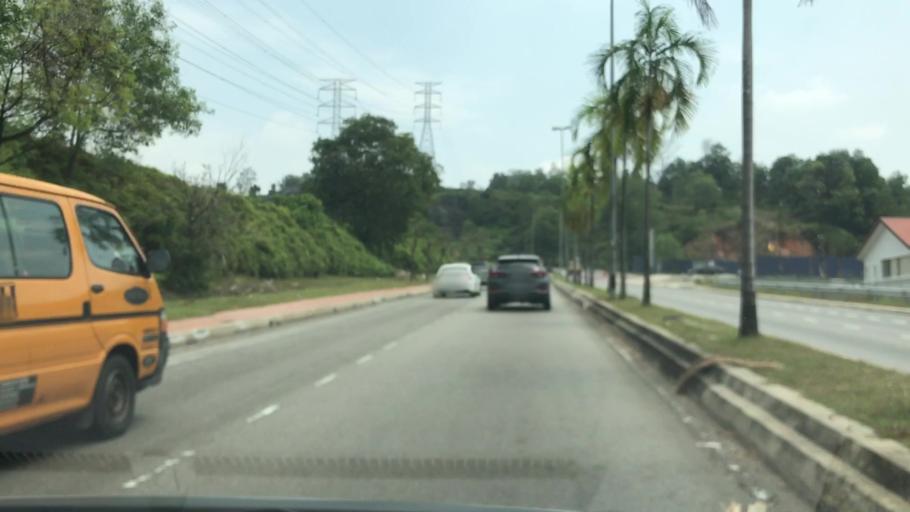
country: MY
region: Selangor
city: Kampong Baharu Balakong
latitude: 3.0388
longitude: 101.6757
